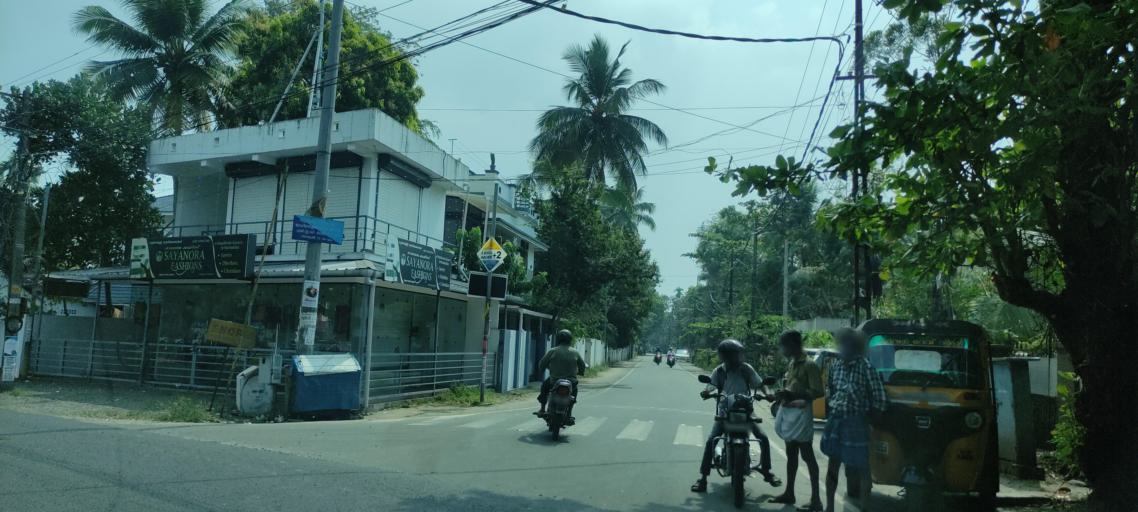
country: IN
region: Kerala
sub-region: Alappuzha
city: Alleppey
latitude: 9.5169
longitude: 76.3339
